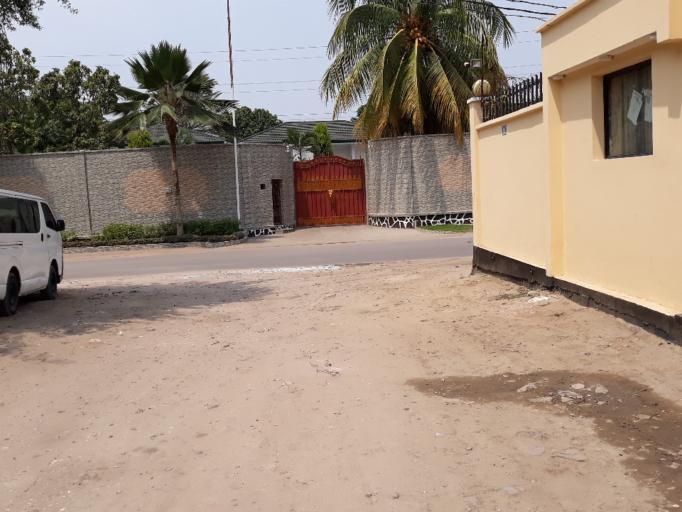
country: CD
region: Kinshasa
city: Kinshasa
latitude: -4.3270
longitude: 15.2791
